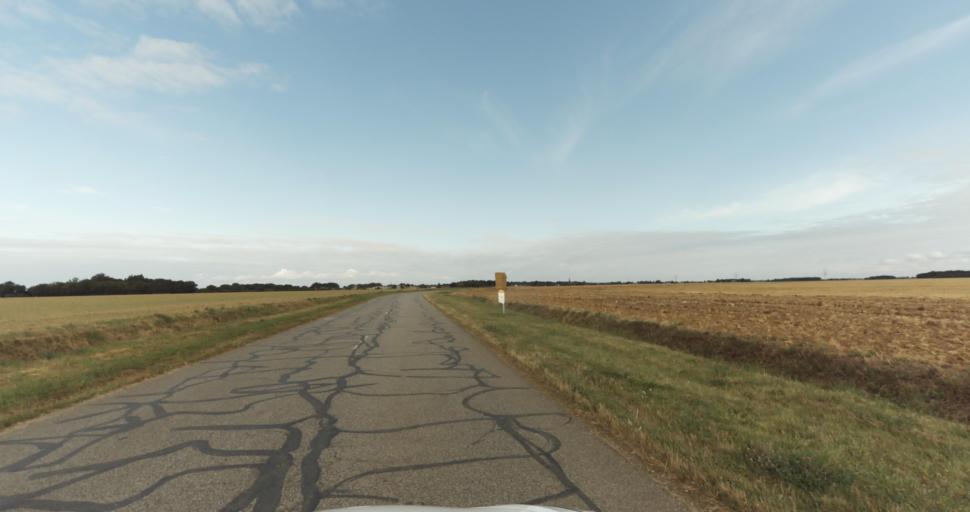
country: FR
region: Haute-Normandie
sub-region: Departement de l'Eure
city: La Madeleine-de-Nonancourt
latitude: 48.8359
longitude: 1.1780
